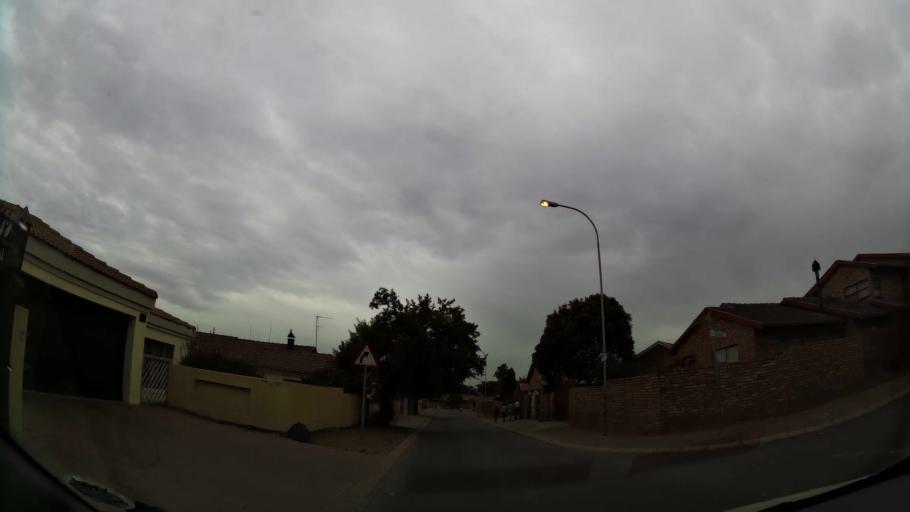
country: ZA
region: Gauteng
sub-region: City of Tshwane Metropolitan Municipality
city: Pretoria
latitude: -25.7204
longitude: 28.3526
